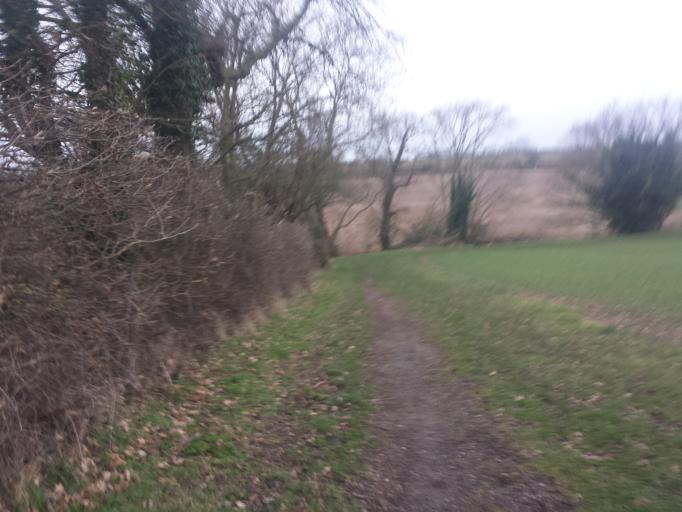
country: GB
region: England
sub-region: Essex
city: Little Clacton
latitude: 51.8517
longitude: 1.1547
